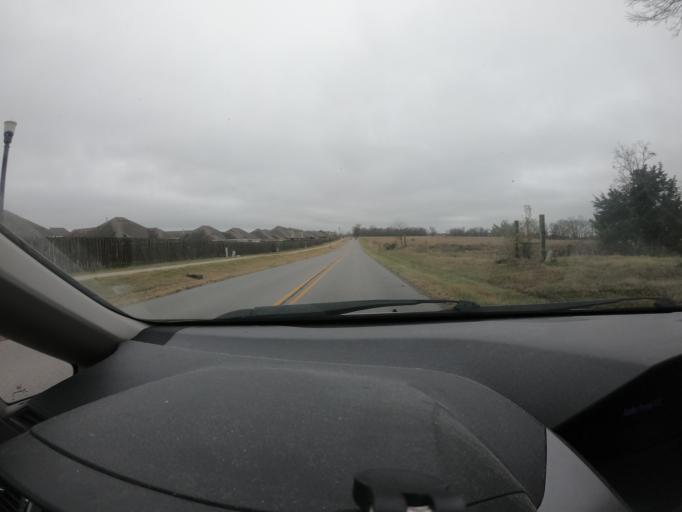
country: US
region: Arkansas
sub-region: Benton County
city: Bentonville
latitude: 36.3498
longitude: -94.2403
